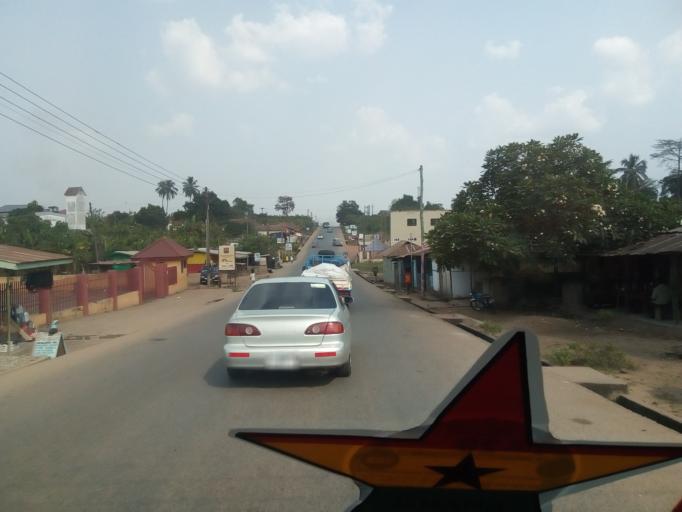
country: GH
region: Eastern
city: Suhum
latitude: 6.0410
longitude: -0.4461
